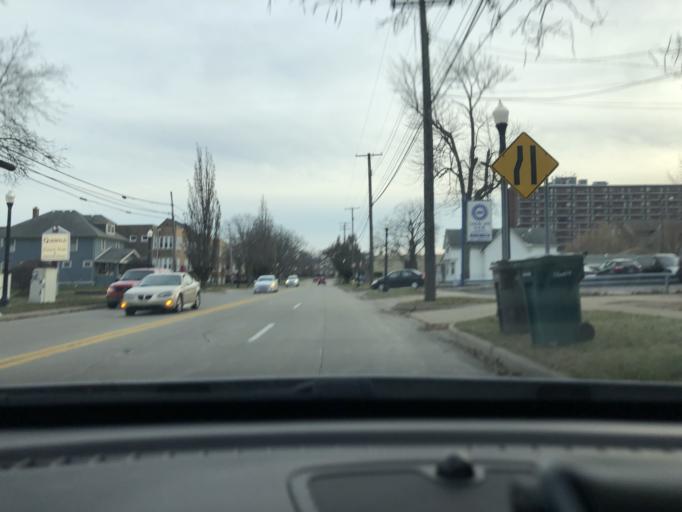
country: US
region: Michigan
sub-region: Wayne County
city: Dearborn Heights
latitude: 42.3041
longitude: -83.2432
